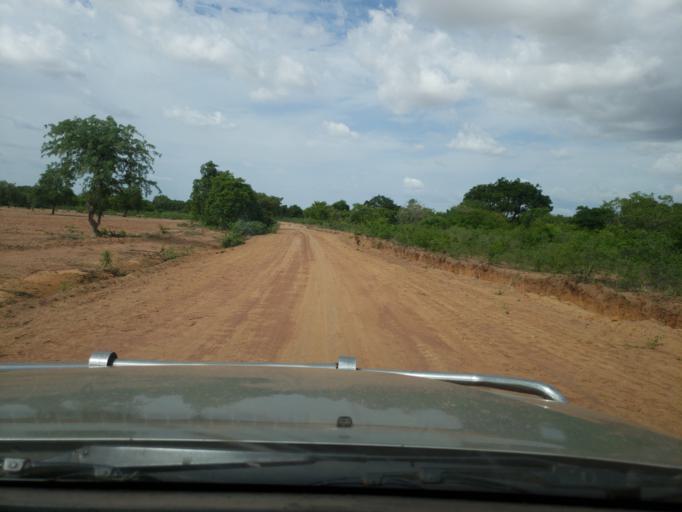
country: ML
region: Segou
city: Bla
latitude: 12.7118
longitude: -5.6878
